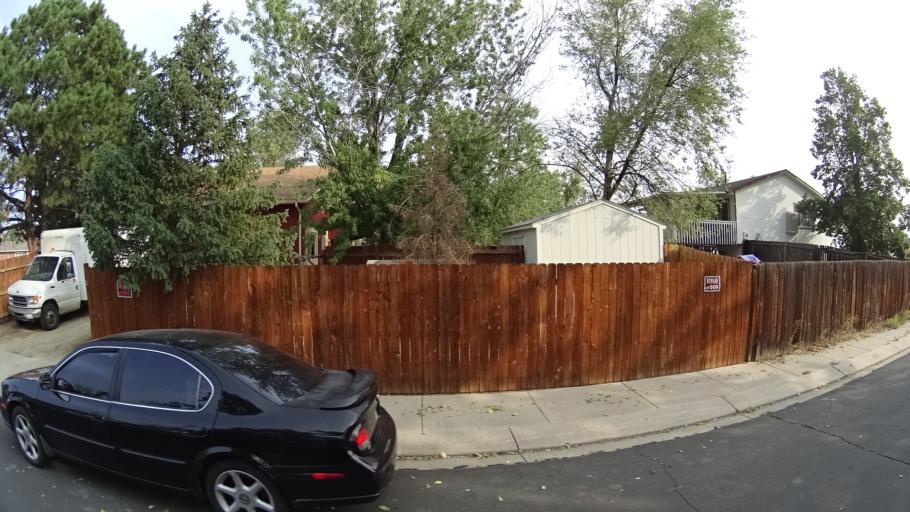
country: US
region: Colorado
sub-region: El Paso County
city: Stratmoor
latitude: 38.8011
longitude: -104.7422
